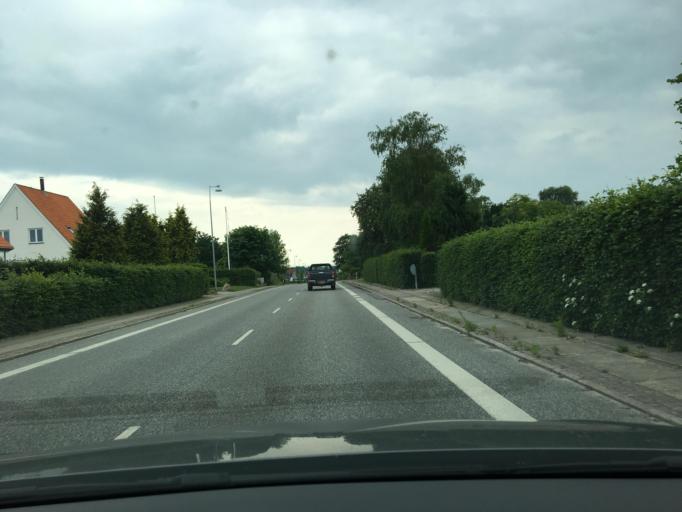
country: DK
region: South Denmark
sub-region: Assens Kommune
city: Assens
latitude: 55.2784
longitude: 9.9148
